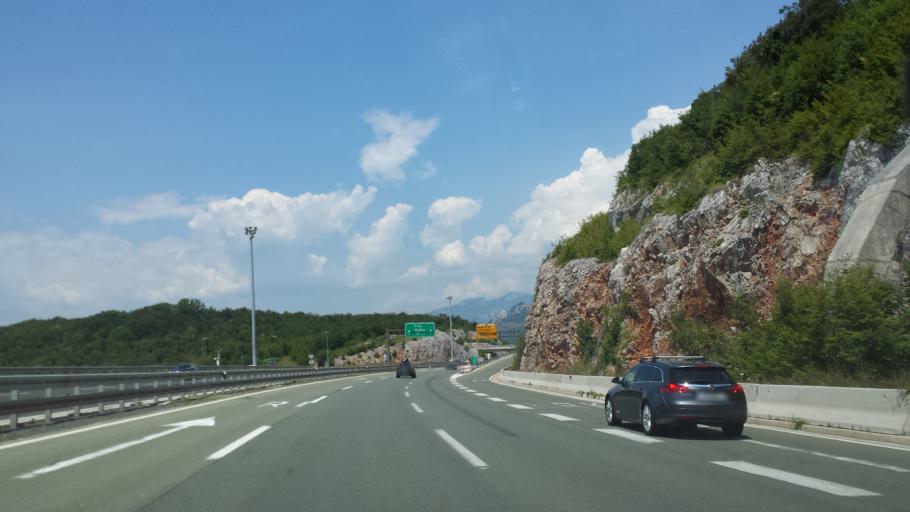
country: HR
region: Primorsko-Goranska
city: Krasica
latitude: 45.3317
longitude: 14.5991
